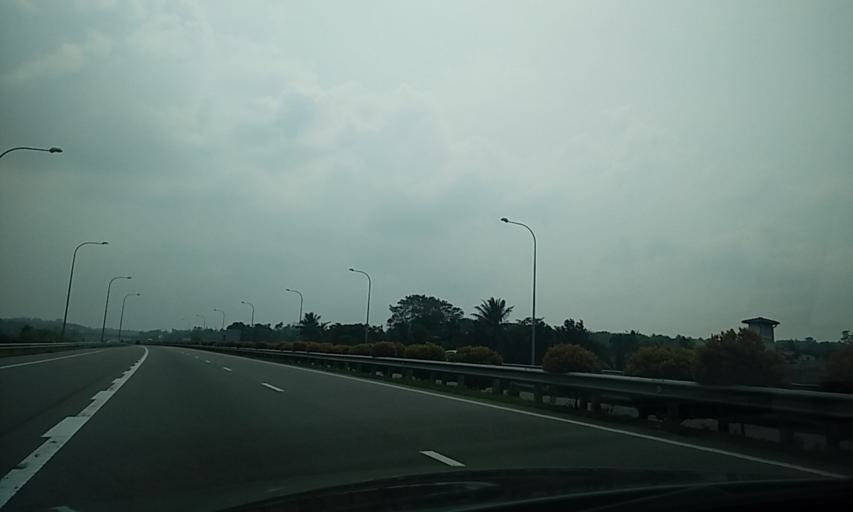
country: LK
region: Western
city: Homagama
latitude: 6.8814
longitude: 79.9768
